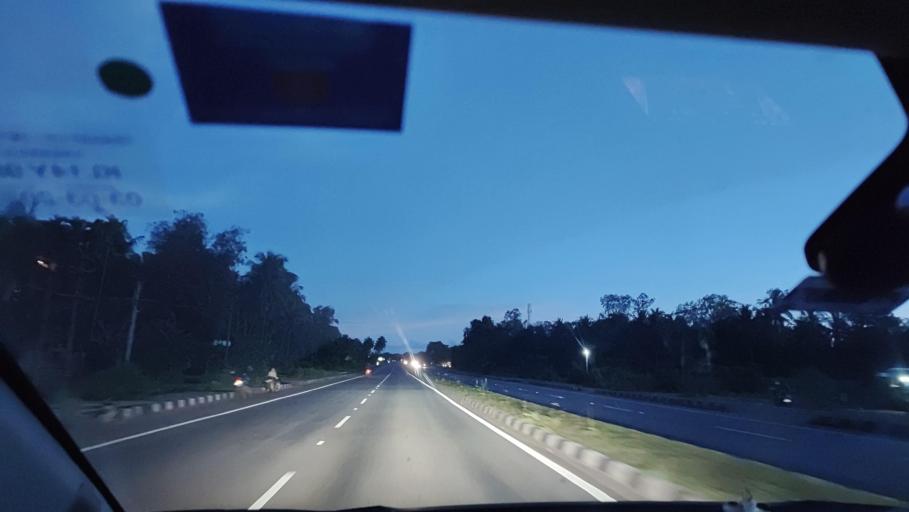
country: IN
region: Karnataka
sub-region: Uttar Kannada
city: Gokarna
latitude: 14.5520
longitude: 74.3925
